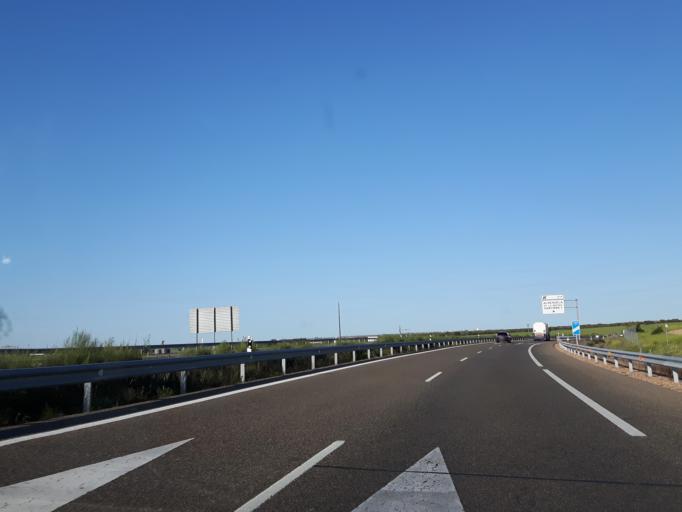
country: ES
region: Castille and Leon
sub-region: Provincia de Salamanca
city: Aldehuela de la Boveda
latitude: 40.8470
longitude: -6.0606
